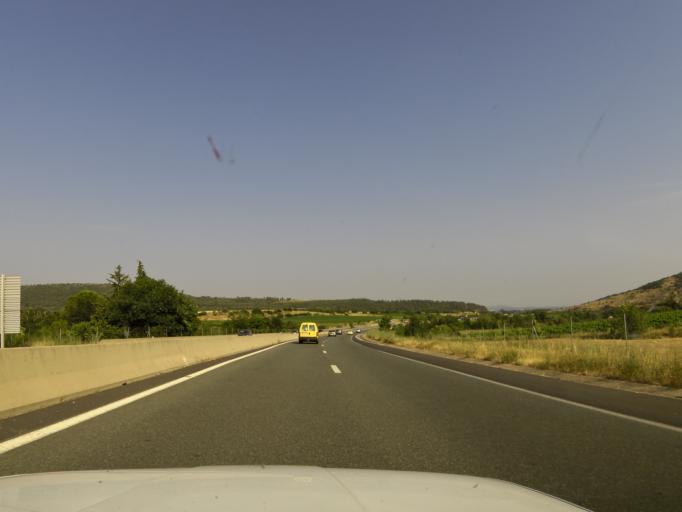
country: FR
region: Languedoc-Roussillon
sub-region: Departement de l'Herault
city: Nebian
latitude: 43.6762
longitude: 3.4200
